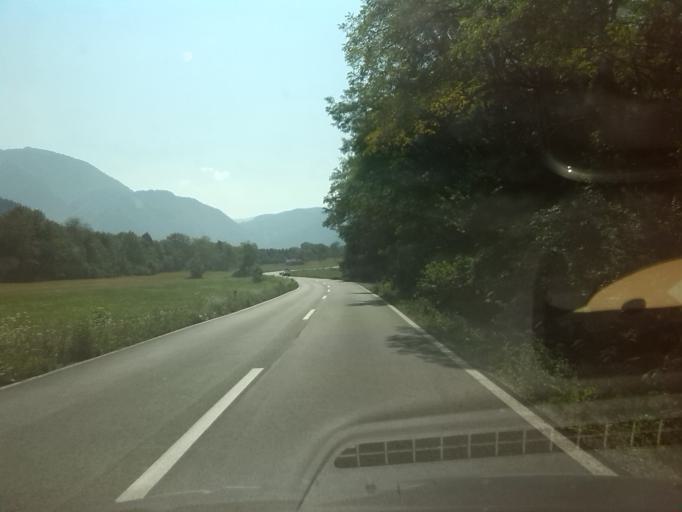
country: SI
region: Tolmin
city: Tolmin
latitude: 46.1900
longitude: 13.7010
